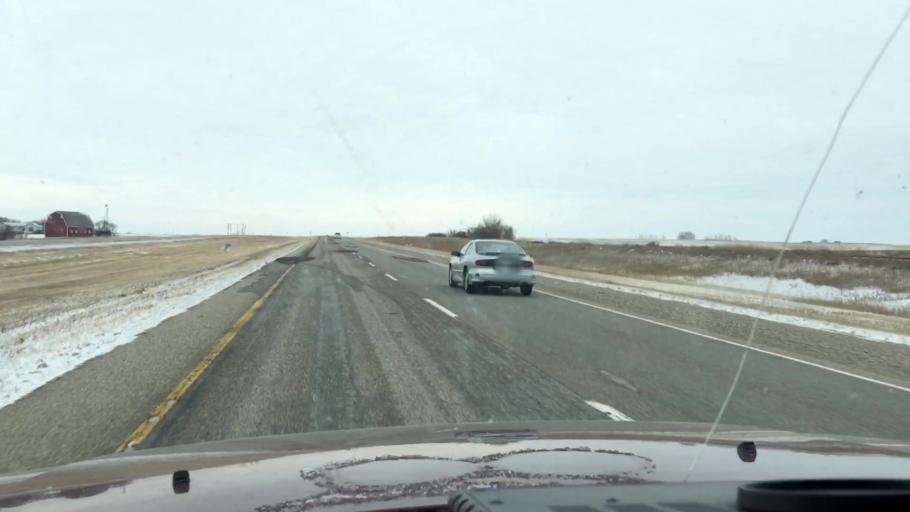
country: CA
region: Saskatchewan
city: Watrous
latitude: 51.4213
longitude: -106.1939
